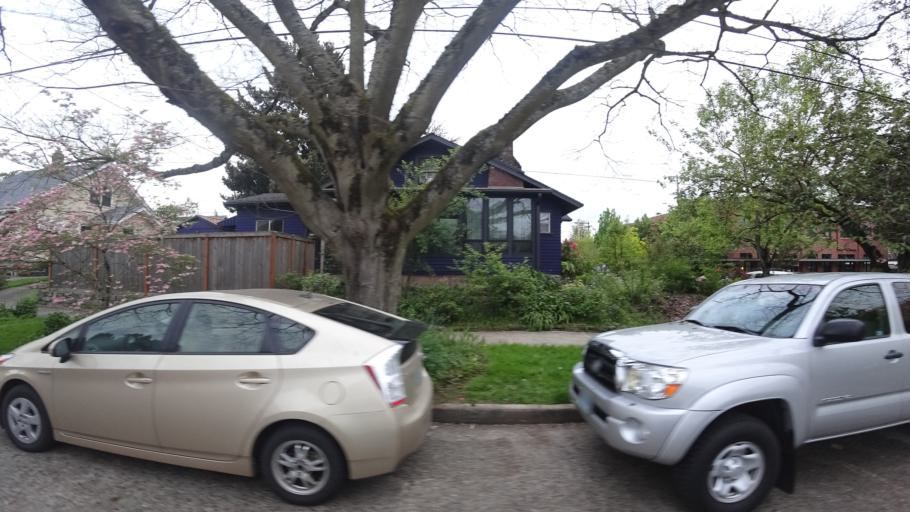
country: US
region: Oregon
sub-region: Clackamas County
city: Milwaukie
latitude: 45.4730
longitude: -122.6503
